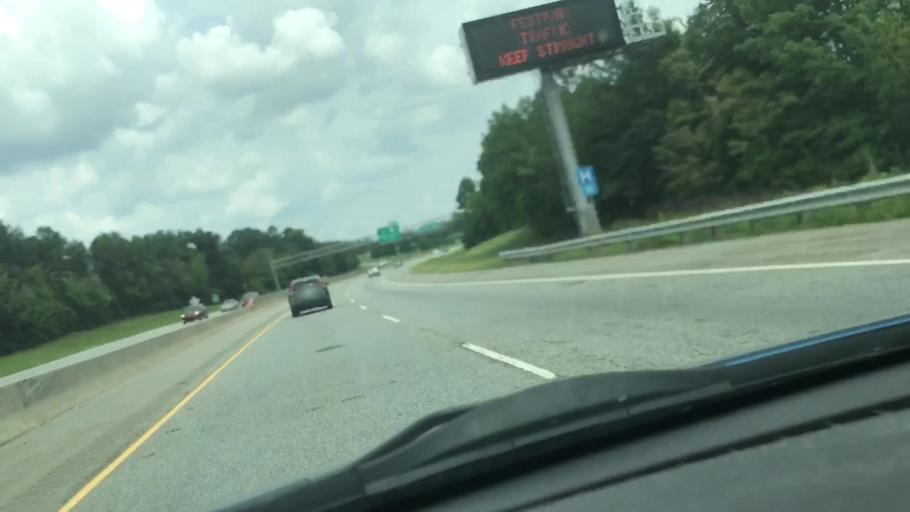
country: US
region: North Carolina
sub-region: Guilford County
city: Greensboro
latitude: 36.0216
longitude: -79.8261
